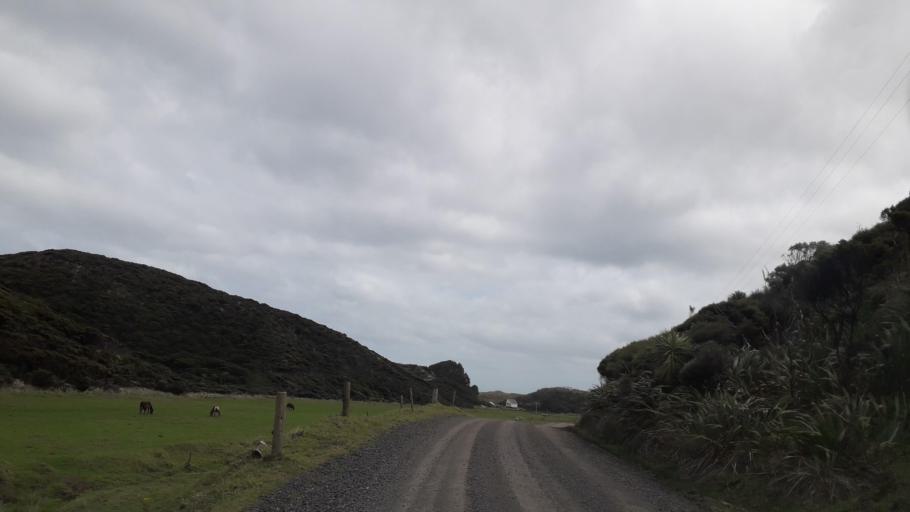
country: NZ
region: Northland
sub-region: Far North District
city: Ahipara
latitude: -35.4404
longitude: 173.2938
